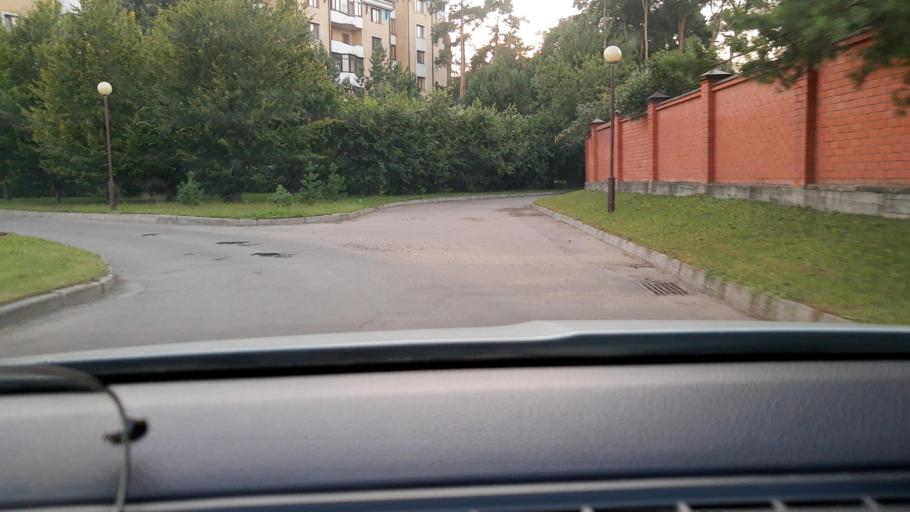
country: RU
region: Moskovskaya
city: Zarech'ye
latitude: 55.6809
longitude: 37.3903
